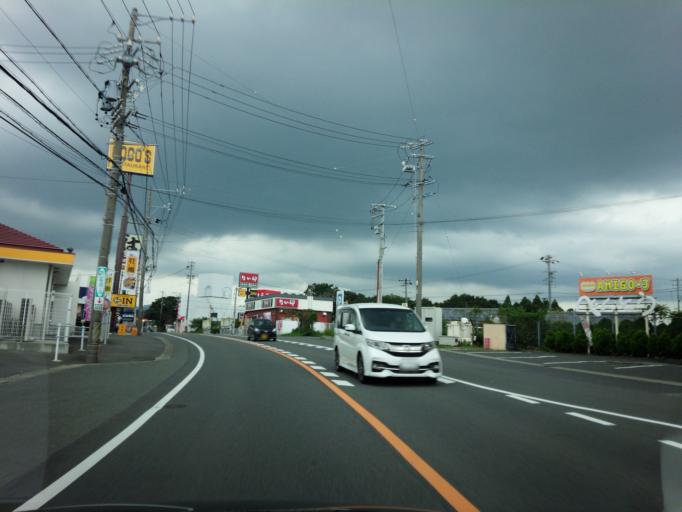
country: JP
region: Mie
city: Toba
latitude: 34.3444
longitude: 136.8156
